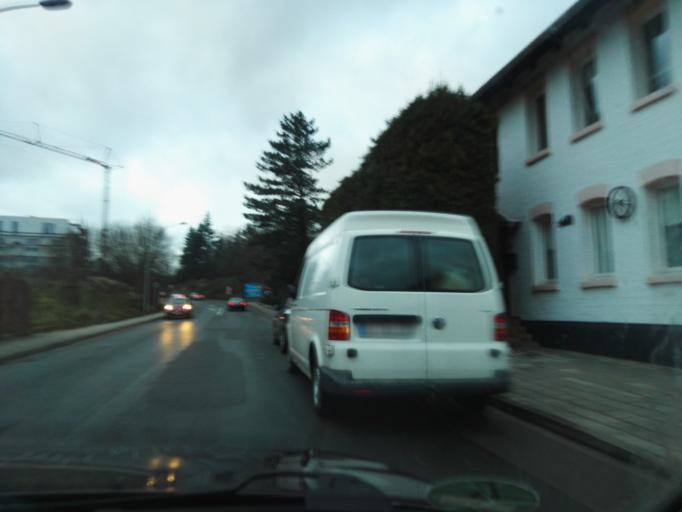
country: DE
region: Lower Saxony
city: Leiferde
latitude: 52.1946
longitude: 10.4723
